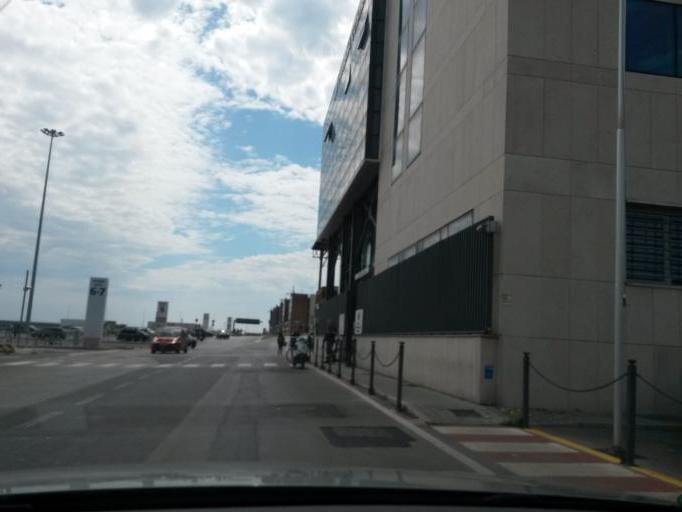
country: IT
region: Tuscany
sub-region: Provincia di Livorno
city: Piombino
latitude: 42.9293
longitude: 10.5445
